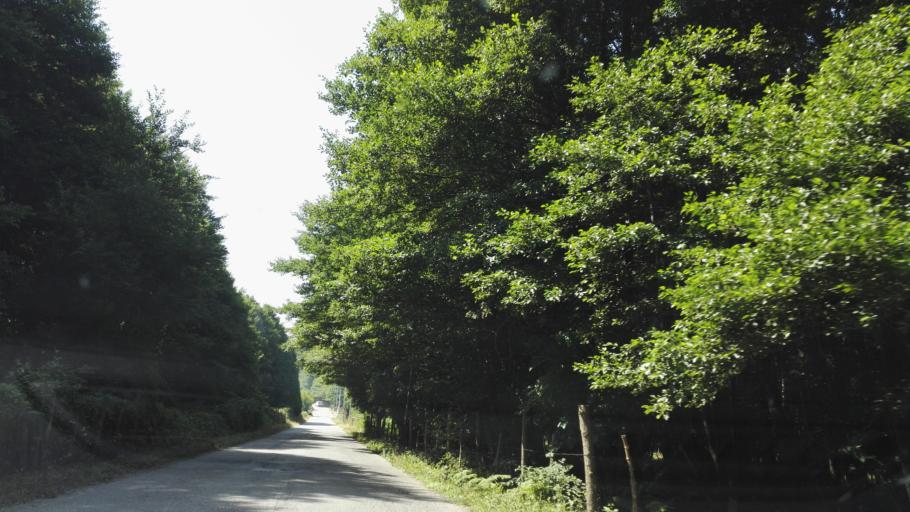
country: IT
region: Calabria
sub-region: Provincia di Vibo-Valentia
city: Mongiana
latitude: 38.5273
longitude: 16.3205
